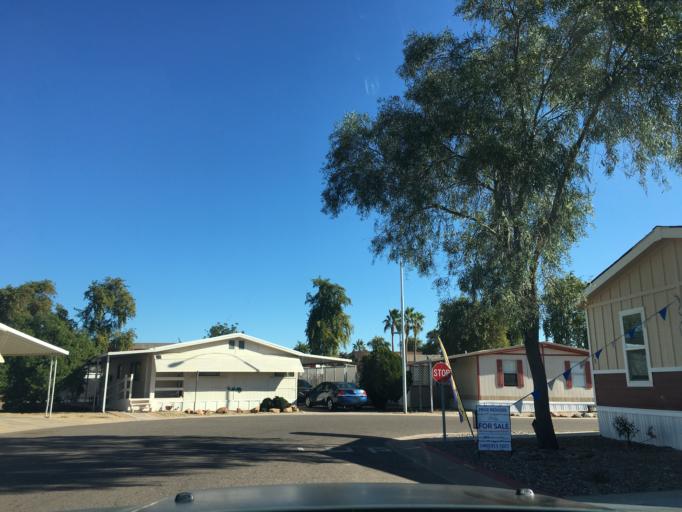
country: US
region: Arizona
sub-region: Maricopa County
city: Mesa
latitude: 33.4509
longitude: -111.8436
